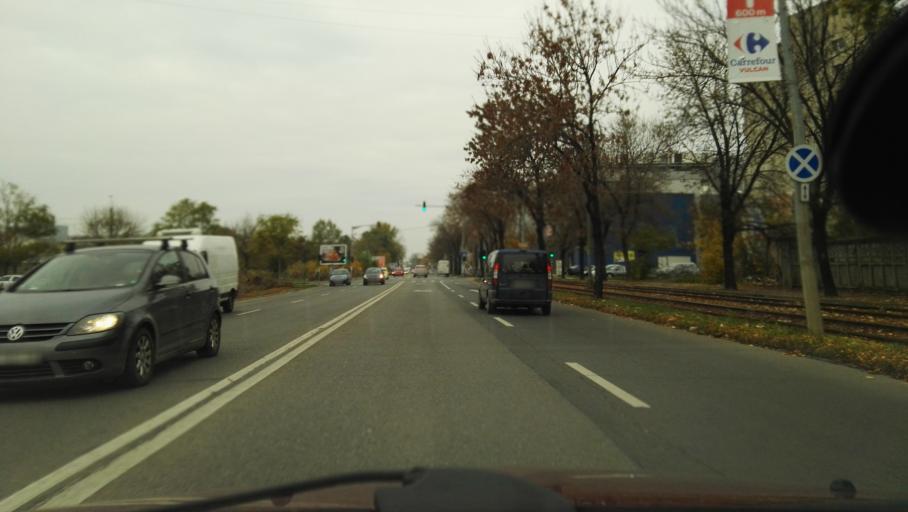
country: RO
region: Bucuresti
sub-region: Municipiul Bucuresti
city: Bucuresti
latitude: 44.4132
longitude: 26.0813
